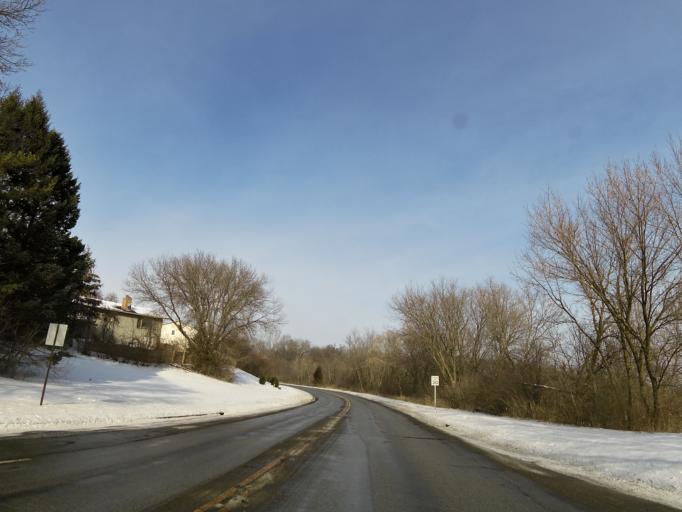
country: US
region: Minnesota
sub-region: Hennepin County
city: Eden Prairie
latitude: 44.8395
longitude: -93.4096
